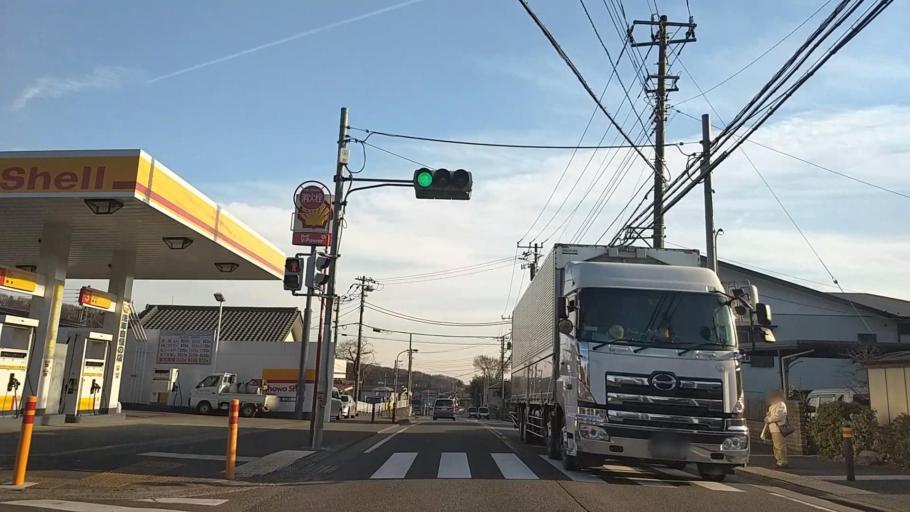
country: JP
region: Kanagawa
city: Zama
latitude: 35.5106
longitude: 139.3033
